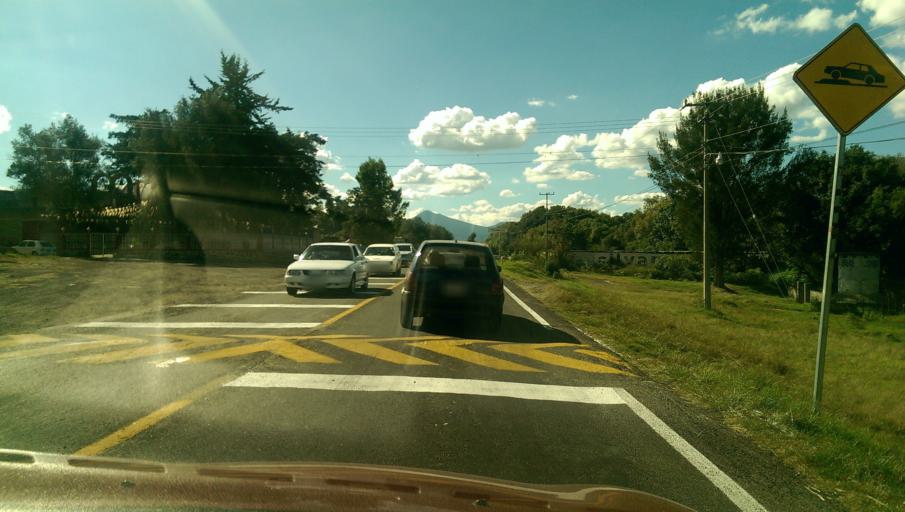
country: MX
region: Michoacan
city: Quiroga
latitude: 19.6397
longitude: -101.5409
